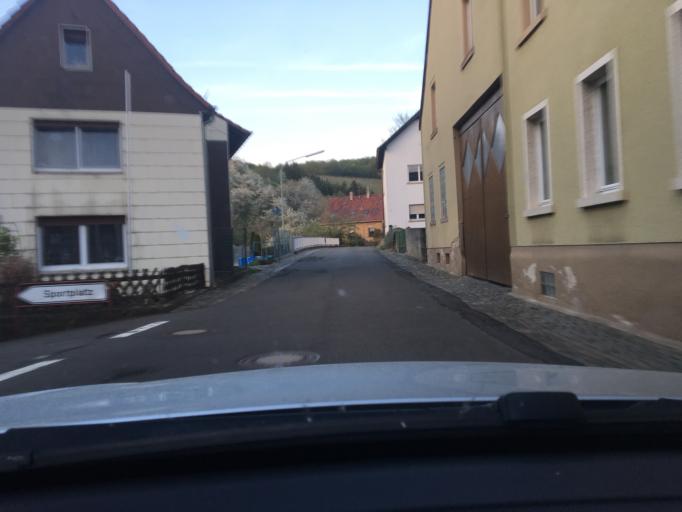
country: DE
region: Rheinland-Pfalz
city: Kalkofen
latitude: 49.7336
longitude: 7.8362
